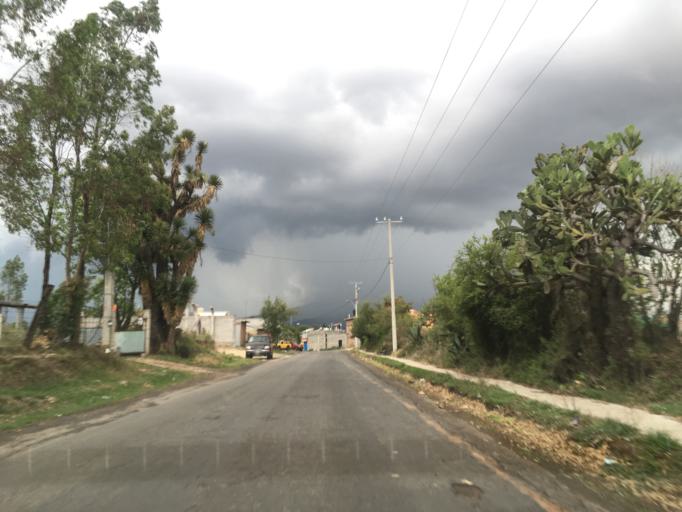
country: MX
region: Michoacan
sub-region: Morelia
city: La Mintzita (Piedra Dura)
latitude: 19.5949
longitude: -101.2755
